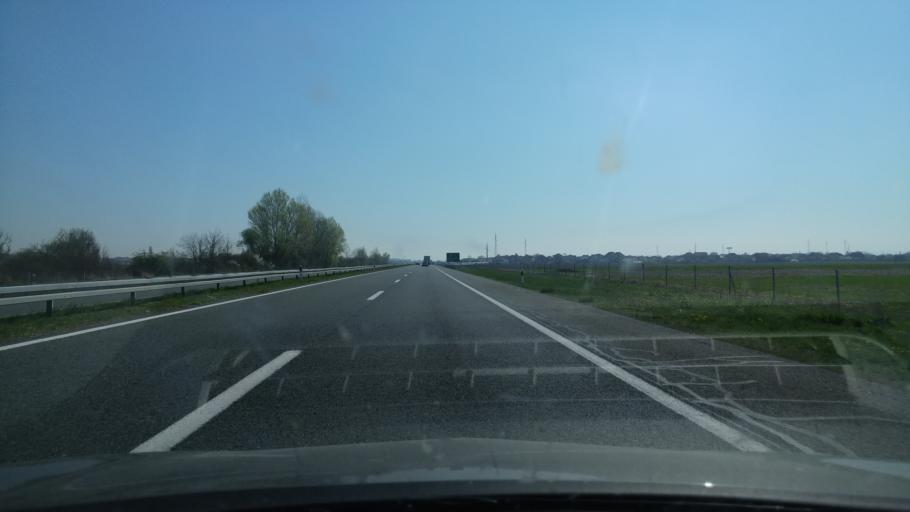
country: HR
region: Brodsko-Posavska
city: Podvinje
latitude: 45.1835
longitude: 18.0373
